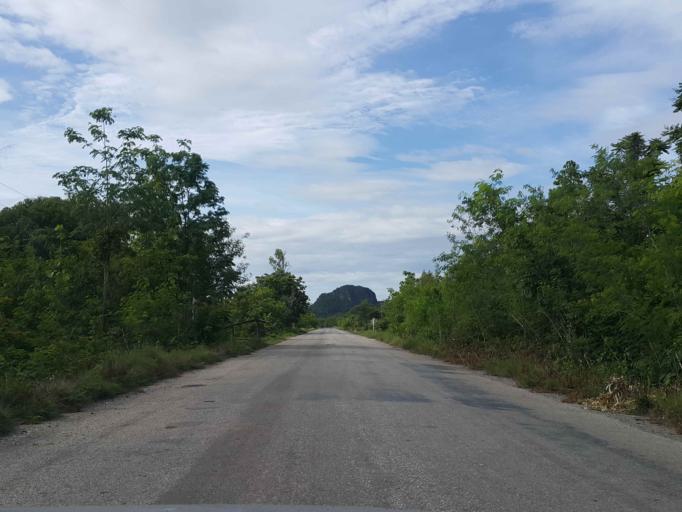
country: TH
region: Sukhothai
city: Thung Saliam
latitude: 17.3006
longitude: 99.5271
